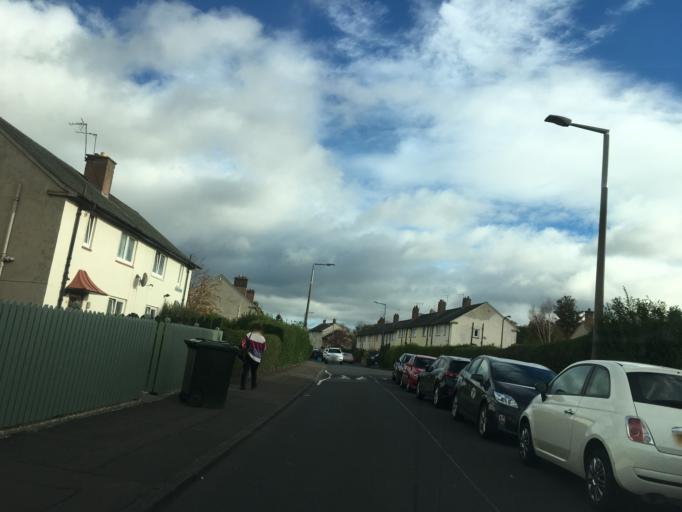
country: GB
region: Scotland
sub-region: Midlothian
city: Loanhead
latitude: 55.9165
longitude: -3.1594
